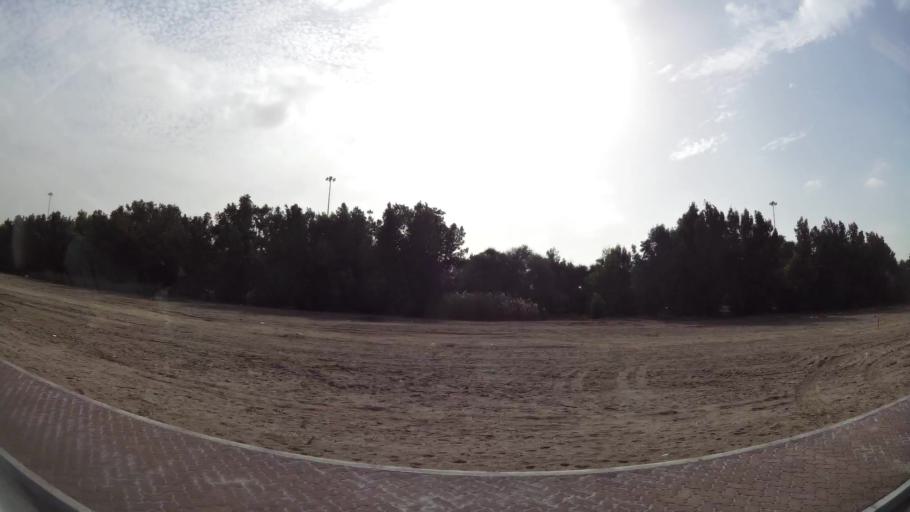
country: AE
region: Abu Dhabi
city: Abu Dhabi
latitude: 24.4030
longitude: 54.5288
